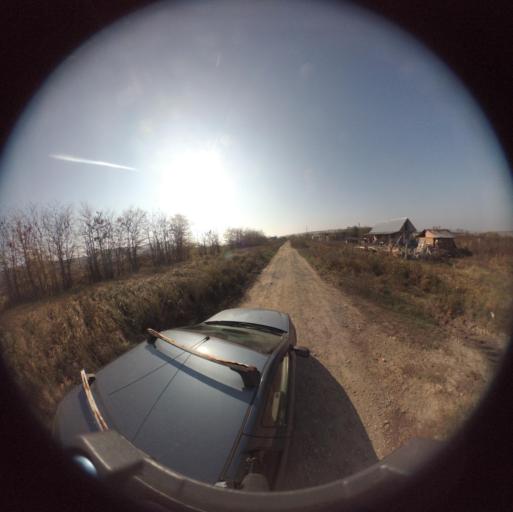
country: RO
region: Vaslui
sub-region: Comuna Bacesti
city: Bacesti
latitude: 46.8292
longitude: 27.2574
